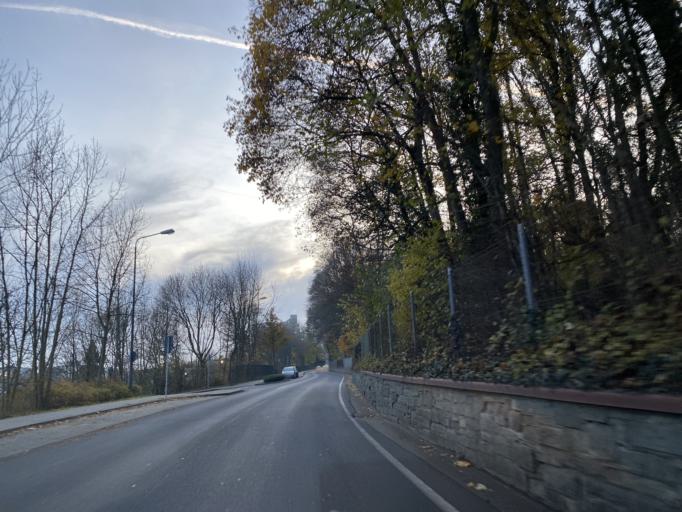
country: DE
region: Hesse
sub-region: Regierungsbezirk Darmstadt
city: Konigstein im Taunus
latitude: 50.1840
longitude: 8.4770
